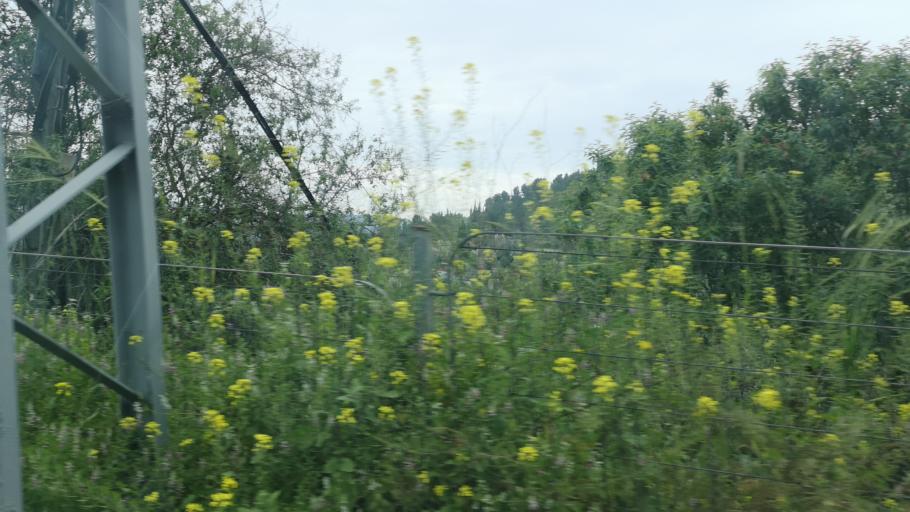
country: PS
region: West Bank
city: Bayt Iksa
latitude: 31.7697
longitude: 35.1613
